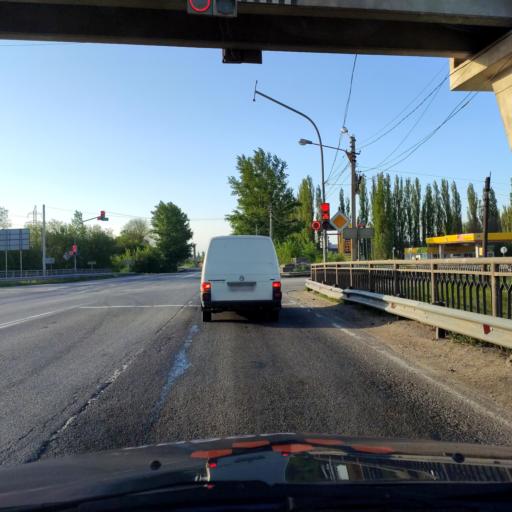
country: RU
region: Lipetsk
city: Yelets
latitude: 52.6001
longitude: 38.4729
